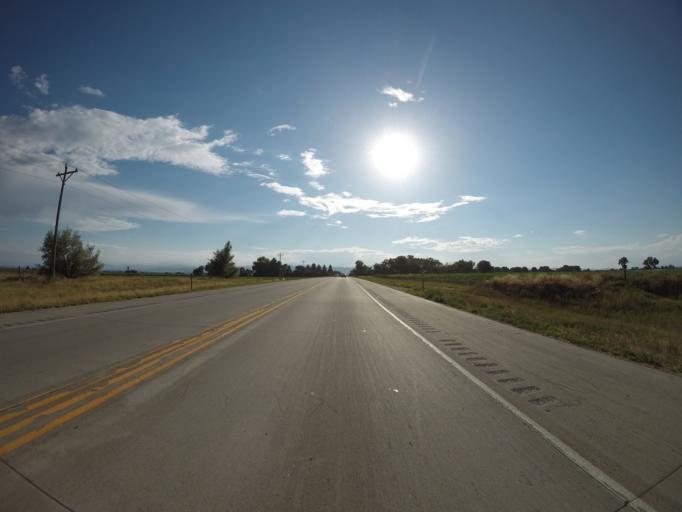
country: US
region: Colorado
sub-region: Weld County
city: Severance
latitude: 40.5810
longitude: -104.9480
